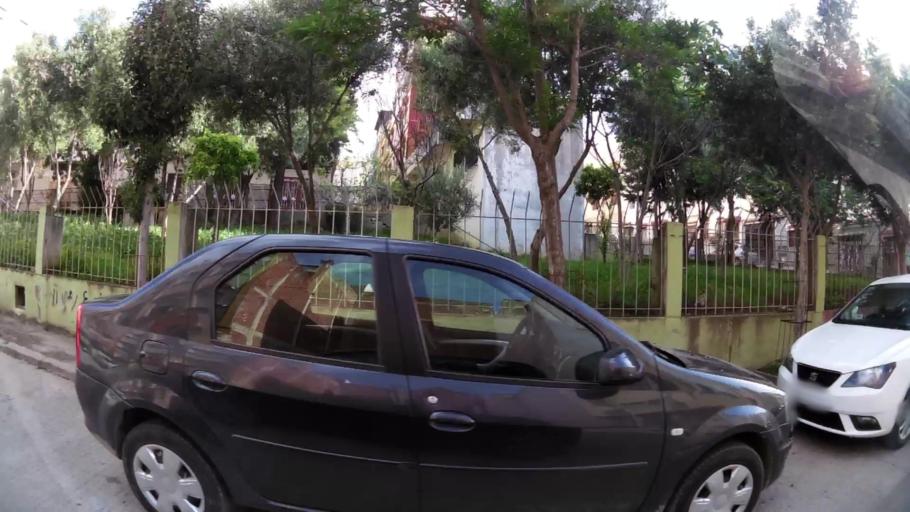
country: MA
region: Tanger-Tetouan
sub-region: Tanger-Assilah
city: Tangier
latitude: 35.7613
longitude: -5.8337
